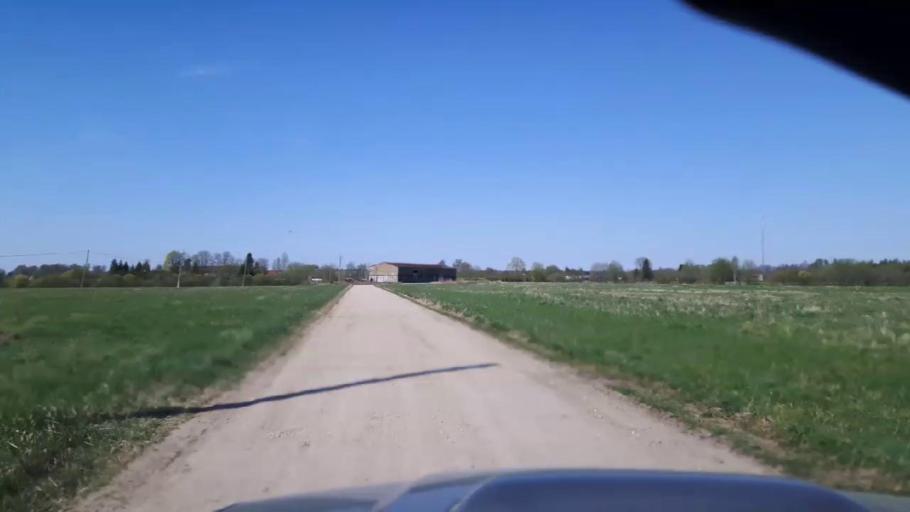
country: EE
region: Paernumaa
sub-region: Sindi linn
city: Sindi
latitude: 58.4451
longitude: 24.7800
